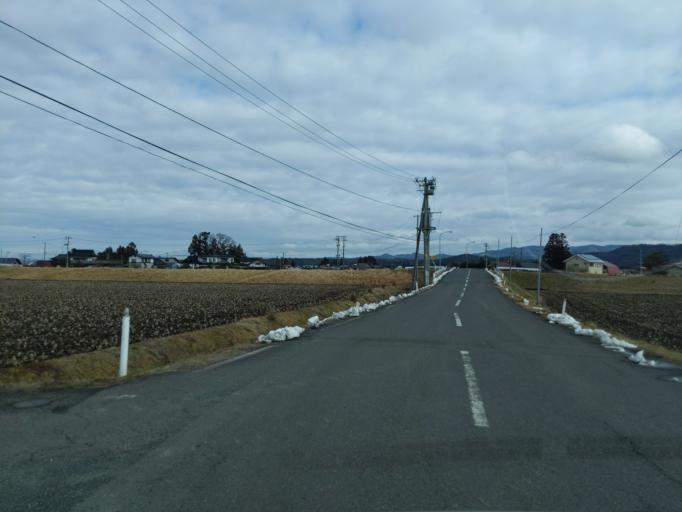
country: JP
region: Iwate
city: Mizusawa
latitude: 39.0815
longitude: 141.1655
